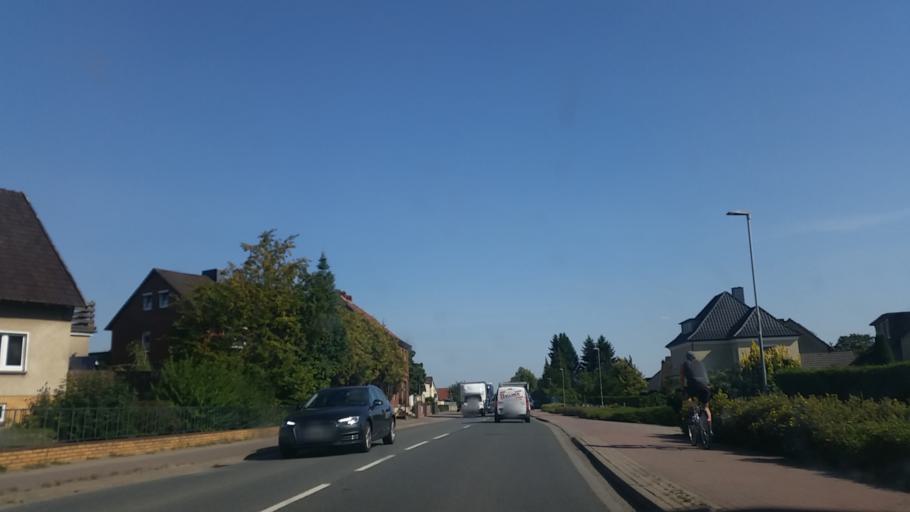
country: DE
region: Lower Saxony
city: Coppenbrugge
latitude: 52.1175
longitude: 9.5518
